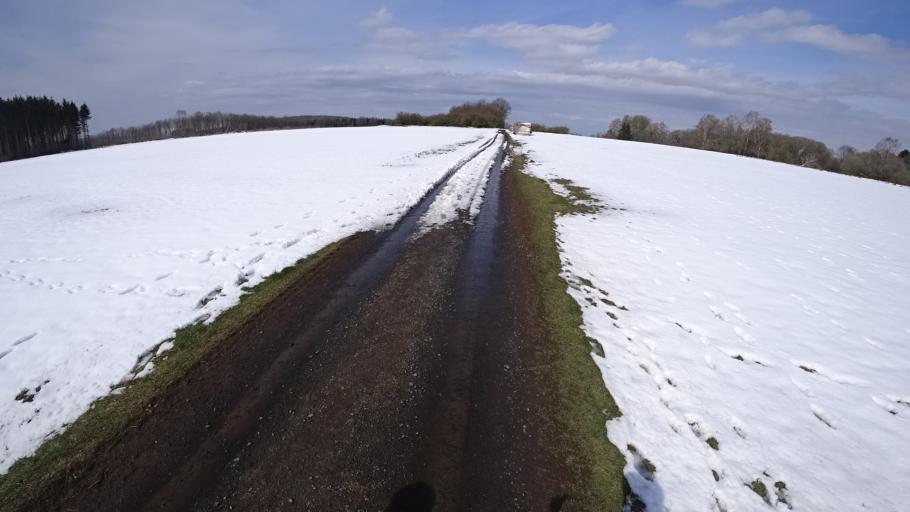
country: DE
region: Rheinland-Pfalz
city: Kausen
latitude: 50.7201
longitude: 7.8592
